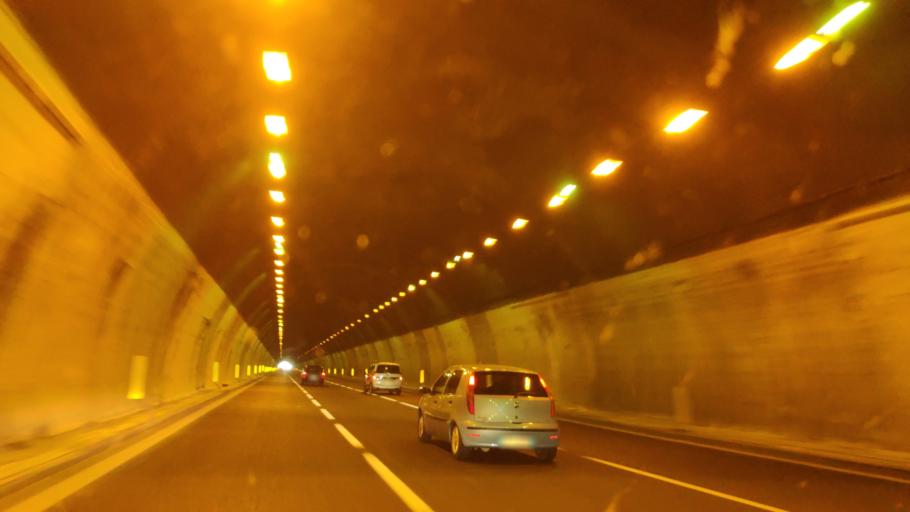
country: IT
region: Campania
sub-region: Provincia di Salerno
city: Lanzara
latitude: 40.7730
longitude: 14.6584
